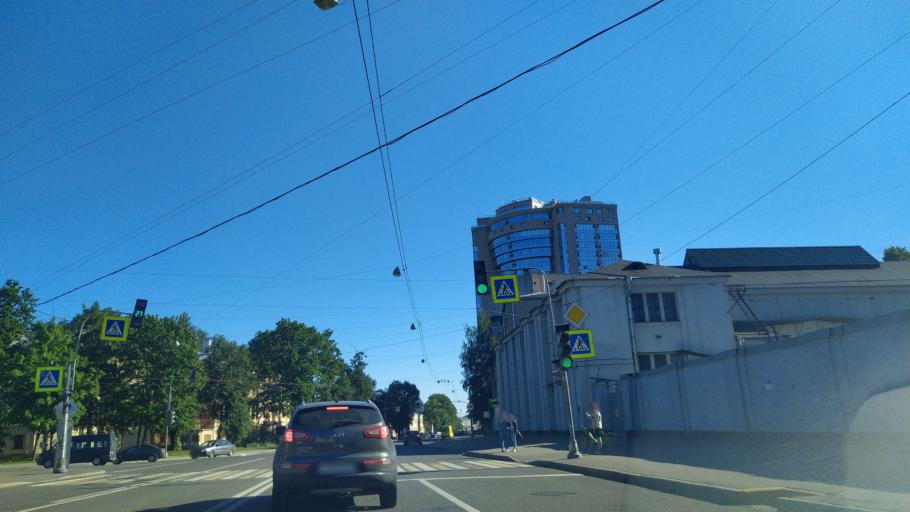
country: RU
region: Leningrad
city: Finlyandskiy
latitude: 59.9596
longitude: 30.3454
